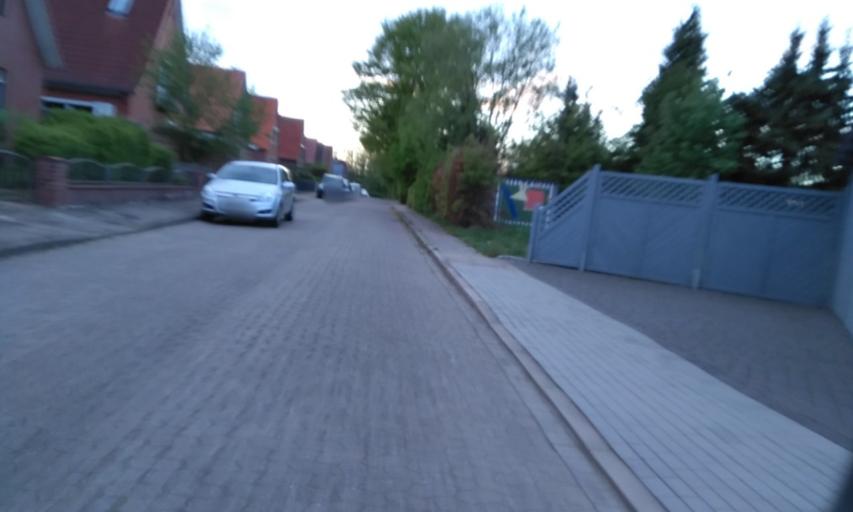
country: DE
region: Lower Saxony
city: Horneburg
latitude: 53.5086
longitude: 9.5703
